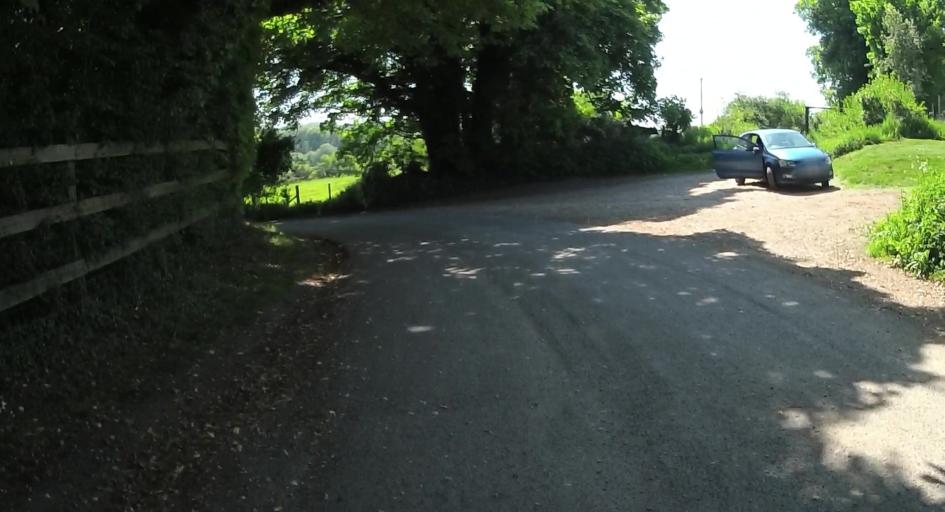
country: GB
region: England
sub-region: Hampshire
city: Kings Worthy
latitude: 51.0912
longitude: -1.1822
